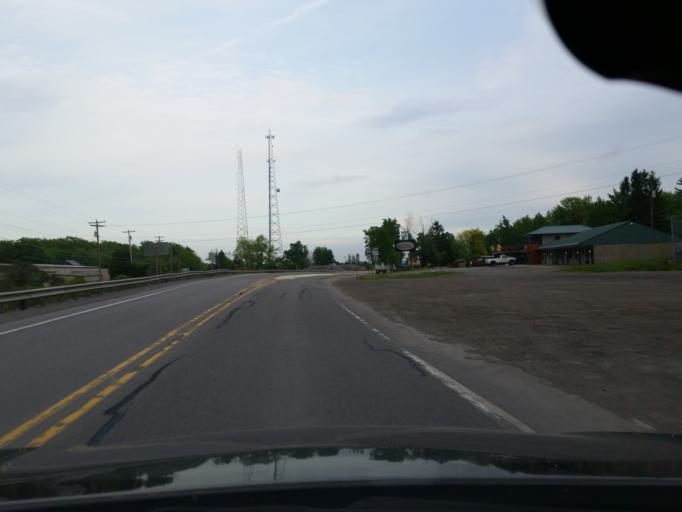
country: US
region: Pennsylvania
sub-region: Elk County
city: Ridgway
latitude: 41.3835
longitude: -78.6876
